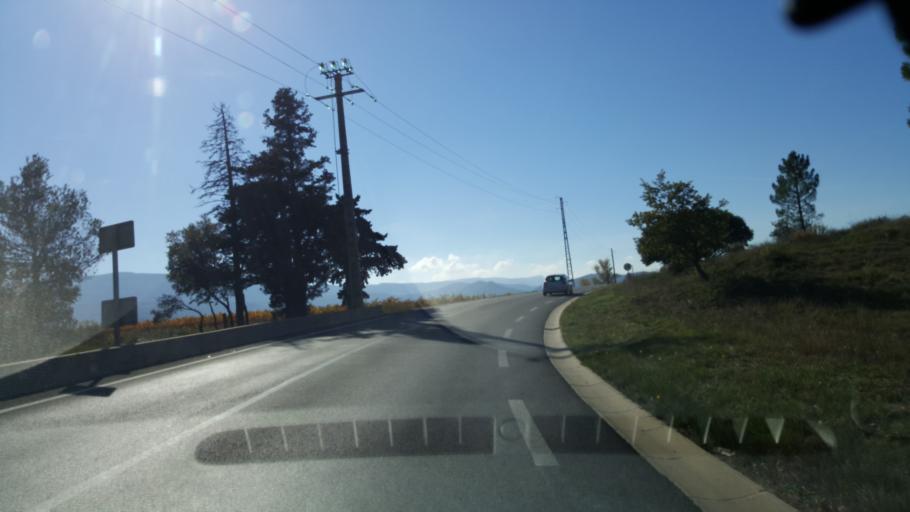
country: FR
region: Provence-Alpes-Cote d'Azur
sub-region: Departement du Var
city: Rougiers
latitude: 43.4074
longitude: 5.8220
